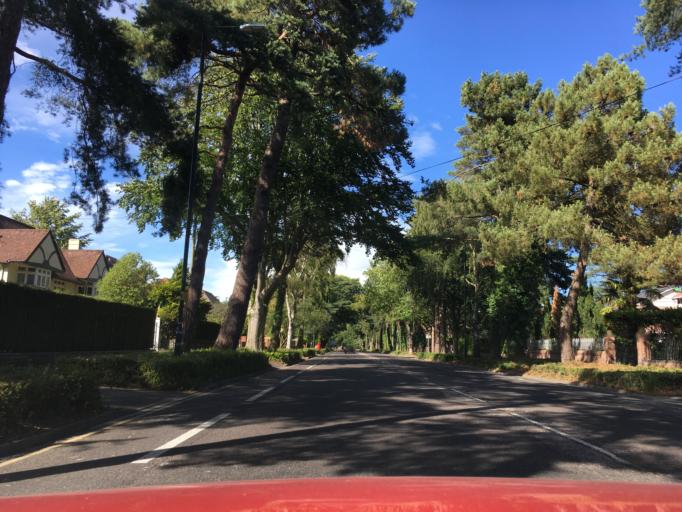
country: GB
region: England
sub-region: Bournemouth
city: Bournemouth
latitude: 50.7367
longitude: -1.8912
